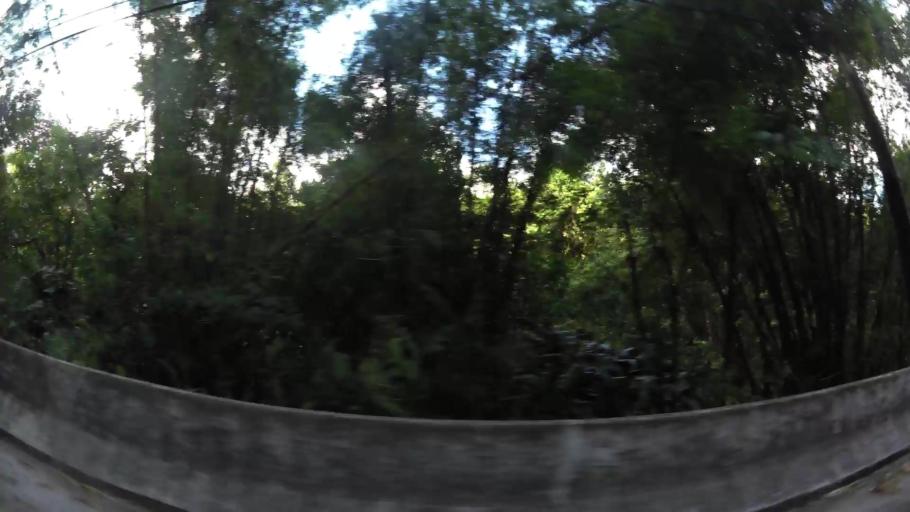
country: MQ
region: Martinique
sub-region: Martinique
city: Saint-Joseph
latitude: 14.6910
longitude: -61.0879
